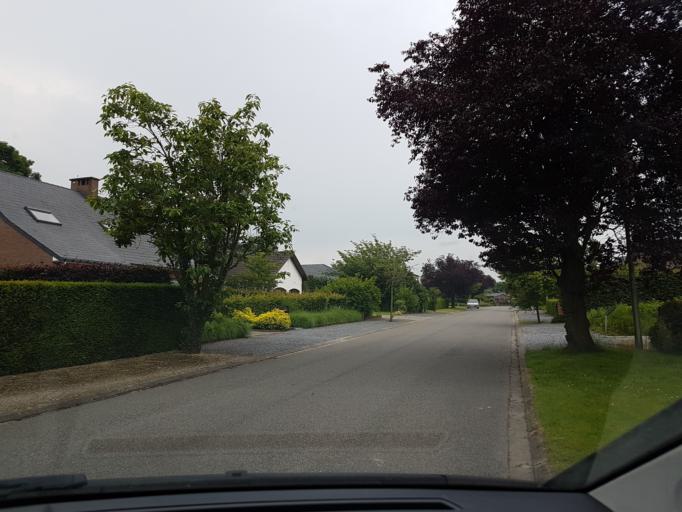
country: BE
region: Flanders
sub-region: Provincie Vlaams-Brabant
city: Steenokkerzeel
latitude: 50.9273
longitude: 4.4916
